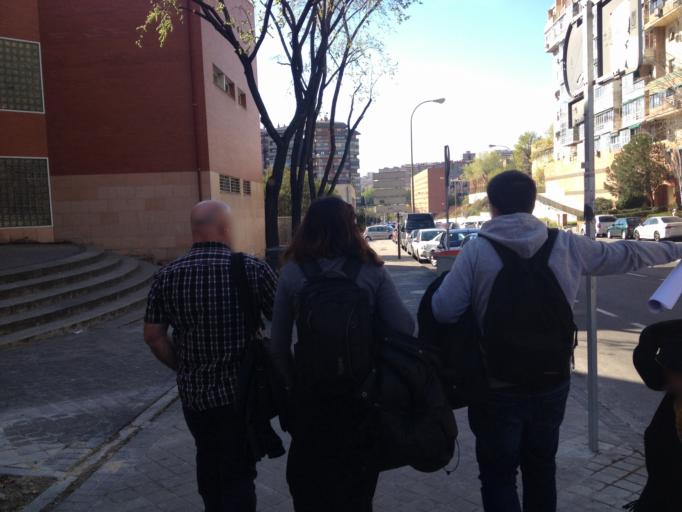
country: ES
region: Madrid
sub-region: Provincia de Madrid
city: Moratalaz
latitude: 40.4124
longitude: -3.6543
